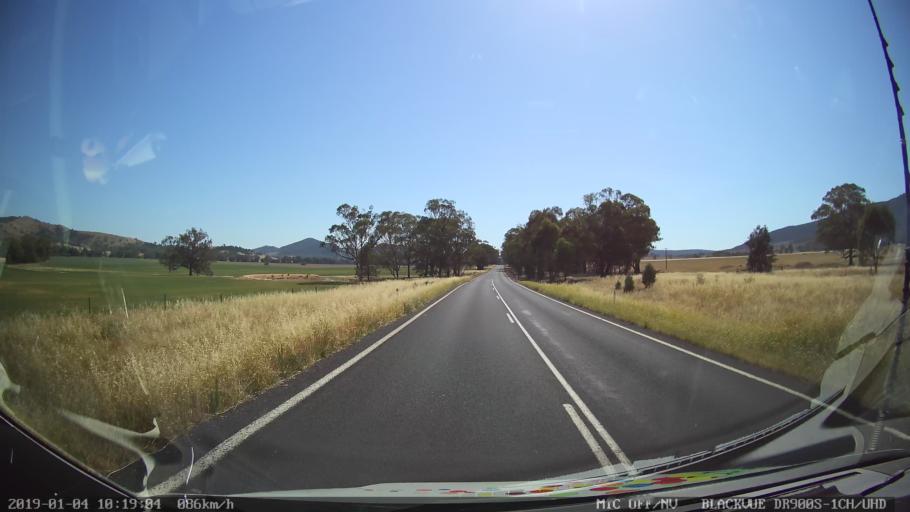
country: AU
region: New South Wales
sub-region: Cabonne
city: Canowindra
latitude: -33.3786
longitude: 148.4752
